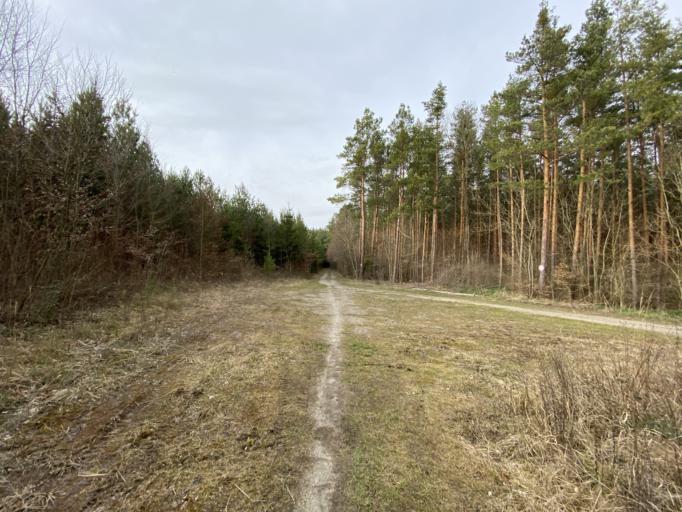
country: AT
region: Lower Austria
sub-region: Politischer Bezirk Modling
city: Gaaden
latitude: 48.0317
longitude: 16.1938
